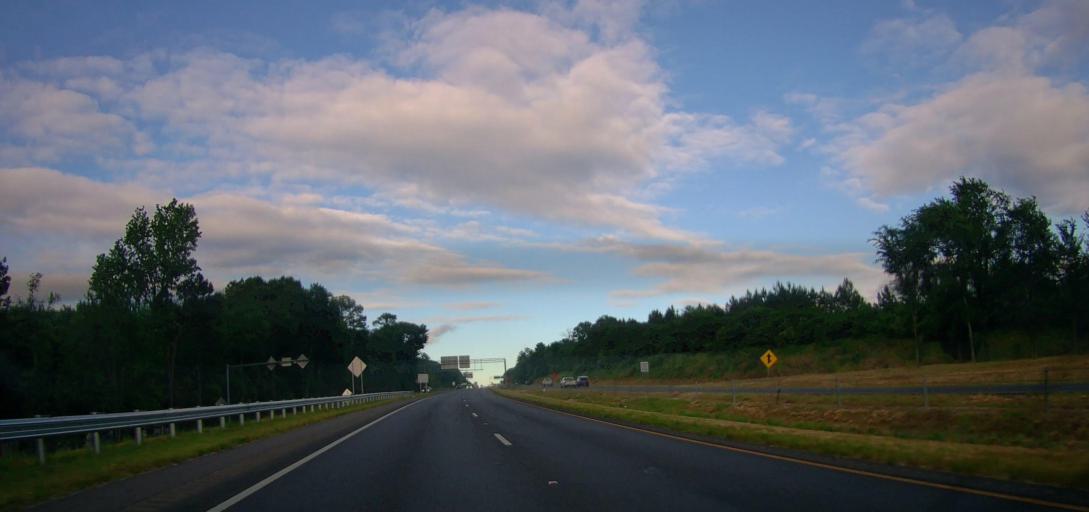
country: US
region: Georgia
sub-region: Clarke County
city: Athens
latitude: 33.9783
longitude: -83.3769
